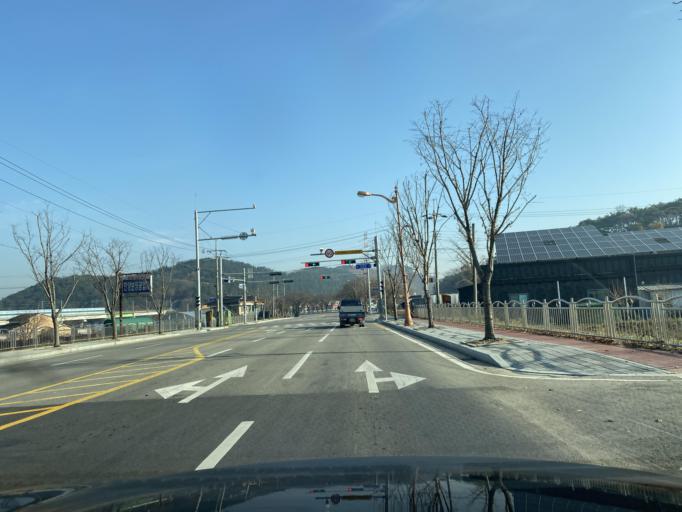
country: KR
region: Chungcheongnam-do
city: Yesan
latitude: 36.7328
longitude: 126.8604
